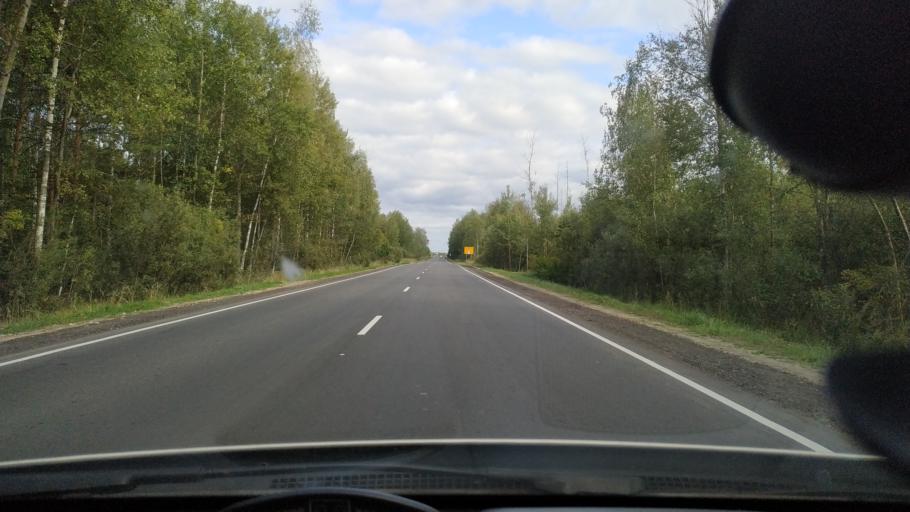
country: RU
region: Moskovskaya
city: Vereya
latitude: 55.7269
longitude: 39.0348
